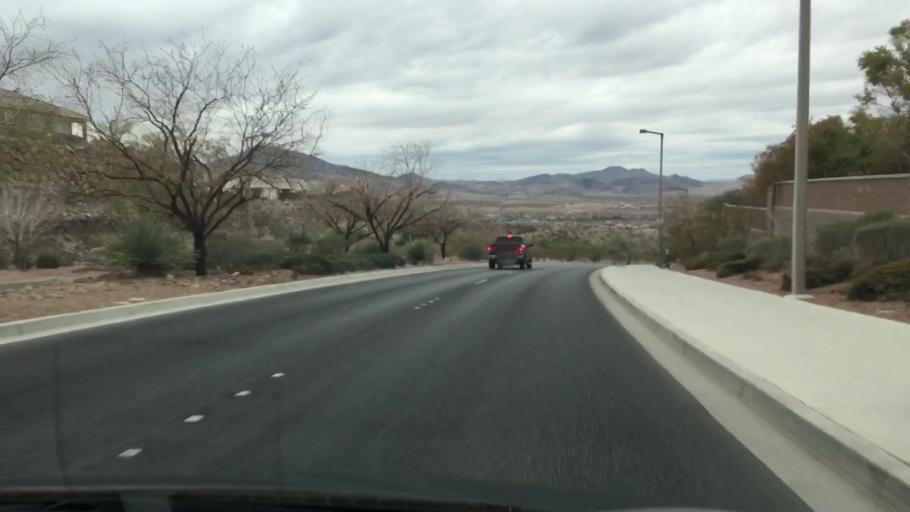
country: US
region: Nevada
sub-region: Clark County
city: Whitney
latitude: 35.9414
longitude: -115.1036
